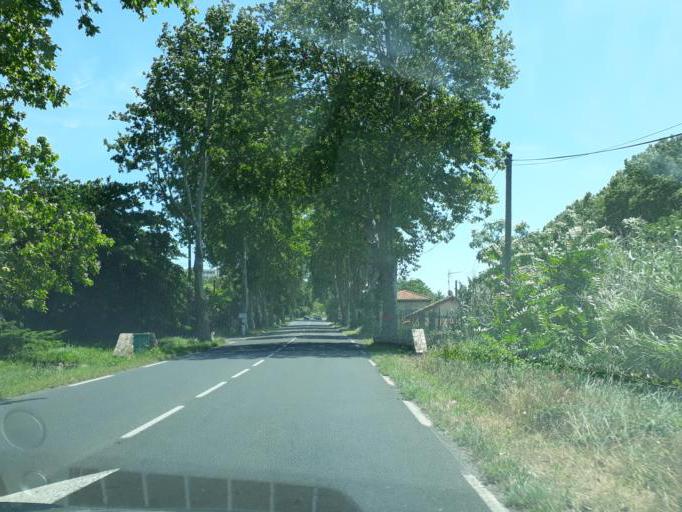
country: FR
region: Languedoc-Roussillon
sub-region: Departement de l'Herault
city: Beziers
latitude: 43.3278
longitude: 3.2436
